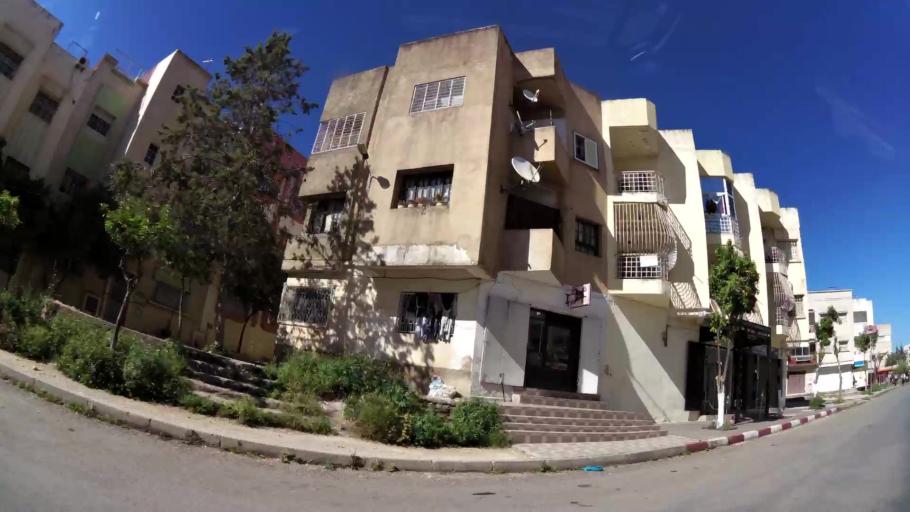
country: MA
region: Fes-Boulemane
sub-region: Fes
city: Fes
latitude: 34.0128
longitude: -4.9752
